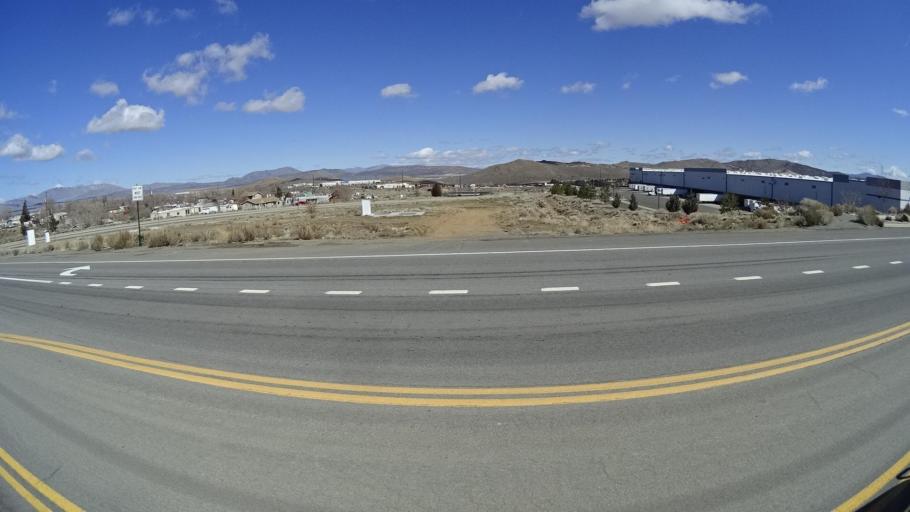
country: US
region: Nevada
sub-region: Washoe County
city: Golden Valley
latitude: 39.6047
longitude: -119.8551
